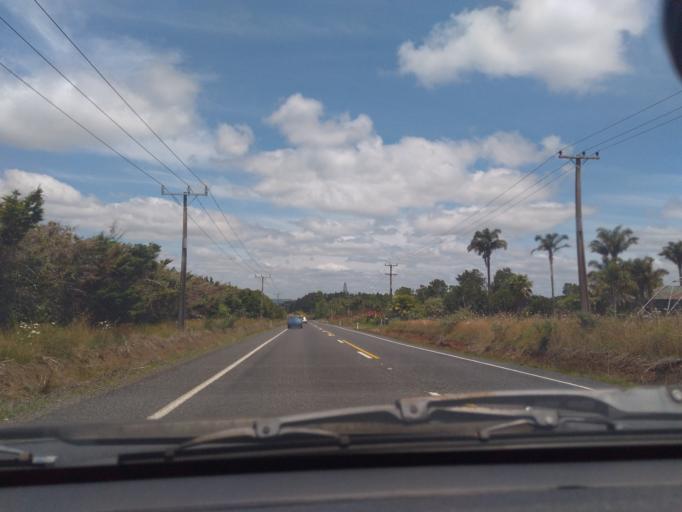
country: NZ
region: Northland
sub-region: Far North District
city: Kerikeri
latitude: -35.1625
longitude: 173.8925
